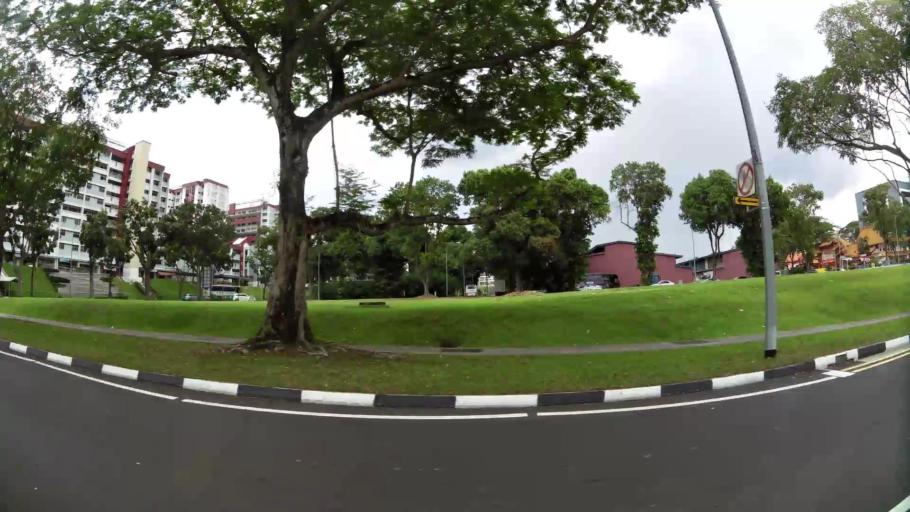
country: MY
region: Johor
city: Johor Bahru
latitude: 1.4383
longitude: 103.7830
